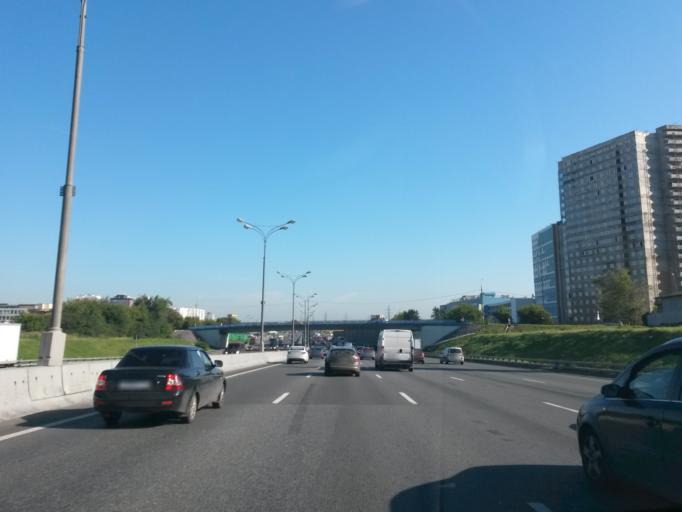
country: RU
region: Moscow
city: Vostochnyy
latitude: 55.8057
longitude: 37.8397
